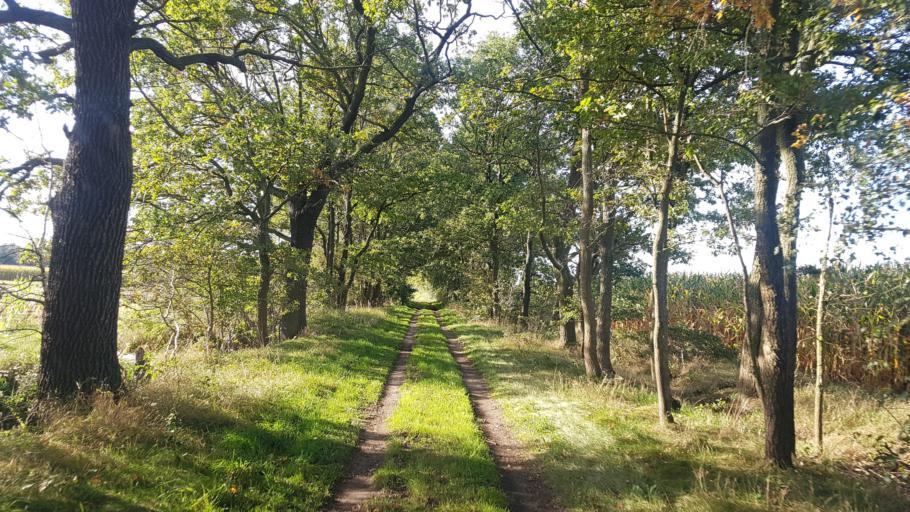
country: DE
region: Brandenburg
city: Schraden
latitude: 51.4244
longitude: 13.7157
